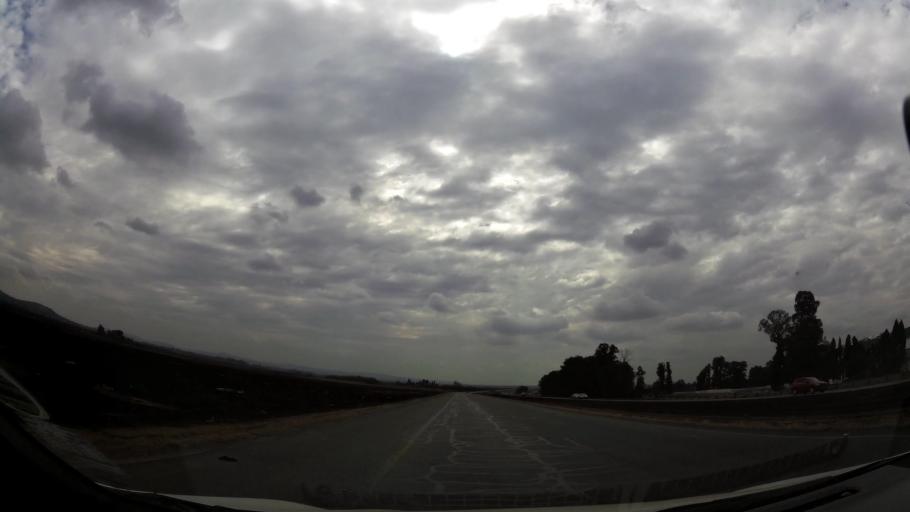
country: ZA
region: Gauteng
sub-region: Sedibeng District Municipality
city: Meyerton
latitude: -26.4076
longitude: 28.0787
